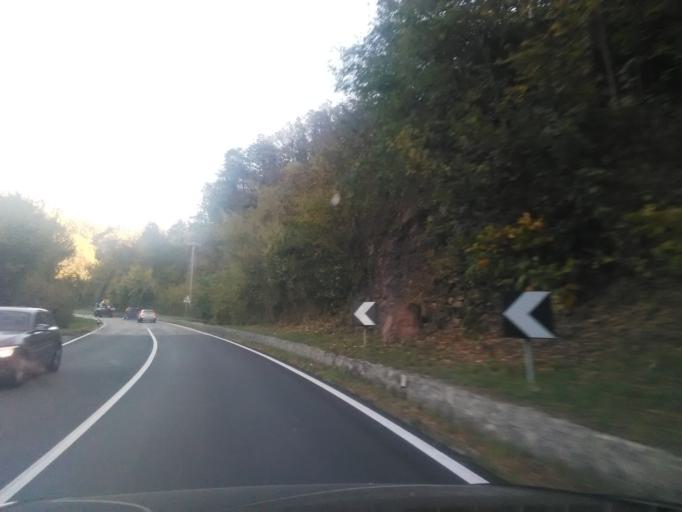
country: IT
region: Piedmont
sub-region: Provincia di Vercelli
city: Guardabosone
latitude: 45.6911
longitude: 8.2676
